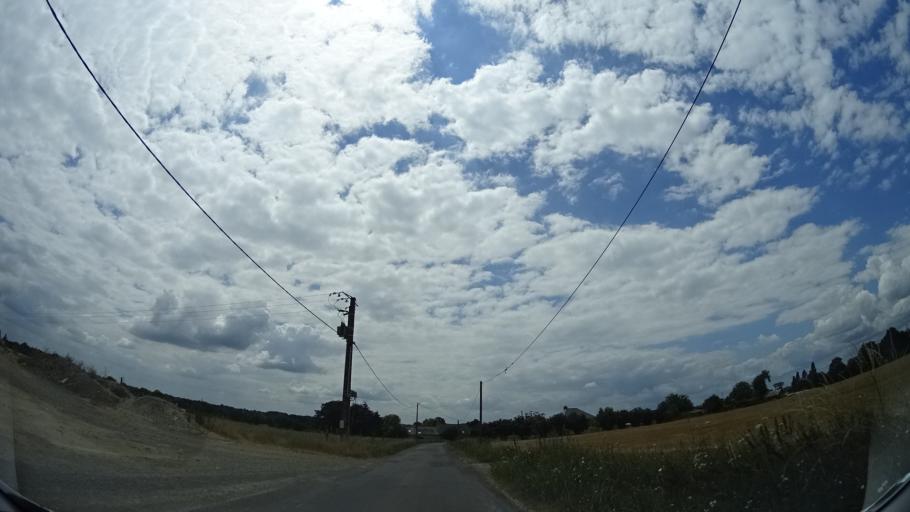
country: FR
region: Brittany
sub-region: Departement d'Ille-et-Vilaine
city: La Chapelle-des-Fougeretz
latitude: 48.1714
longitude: -1.7540
